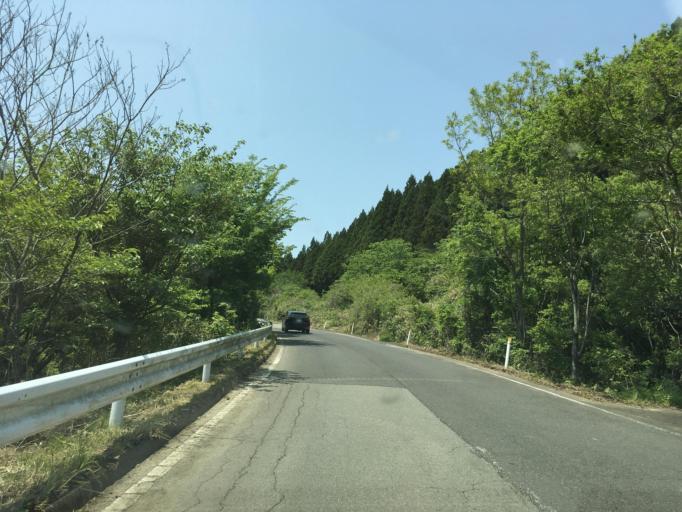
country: JP
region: Iwate
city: Ofunato
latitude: 38.8523
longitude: 141.4977
